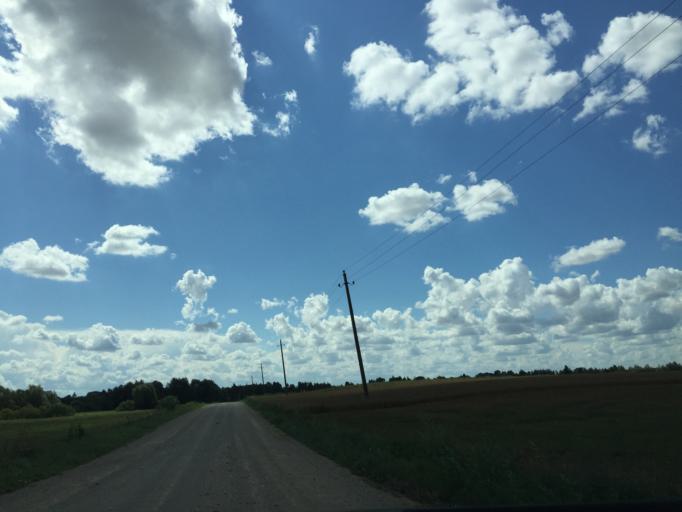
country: LV
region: Rundales
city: Pilsrundale
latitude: 56.2842
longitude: 23.9964
